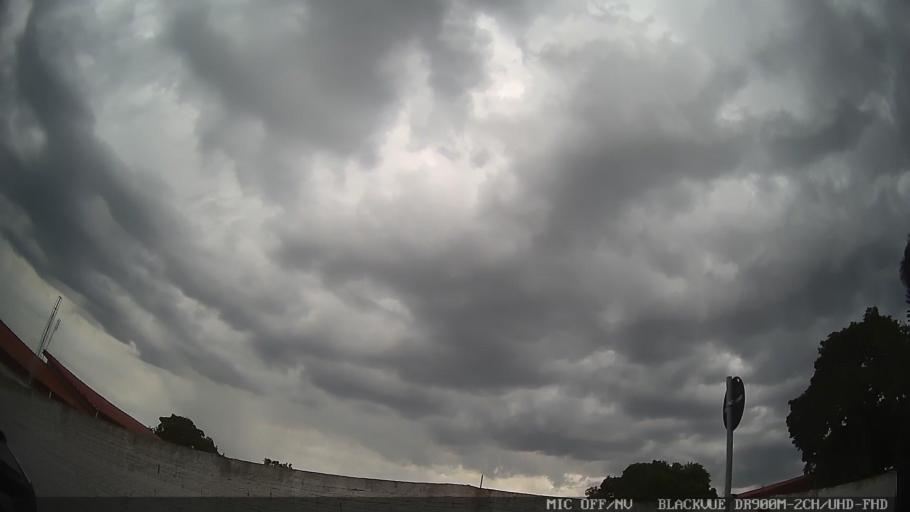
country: BR
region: Sao Paulo
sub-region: Amparo
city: Amparo
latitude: -22.7033
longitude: -46.7662
